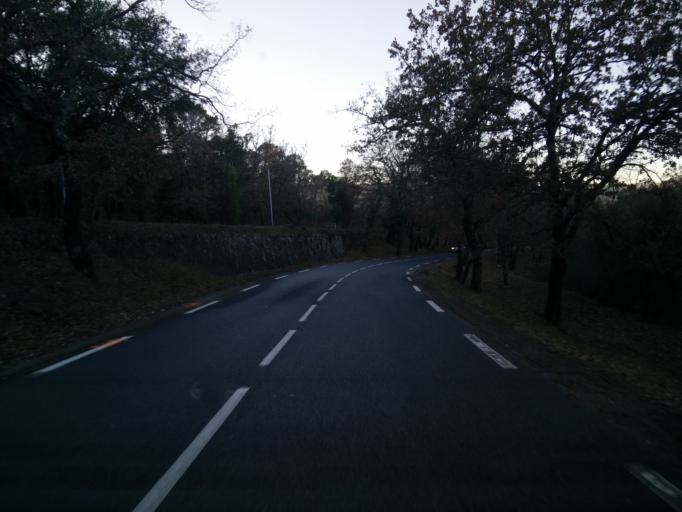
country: FR
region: Provence-Alpes-Cote d'Azur
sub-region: Departement du Var
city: Figanieres
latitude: 43.5505
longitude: 6.5275
